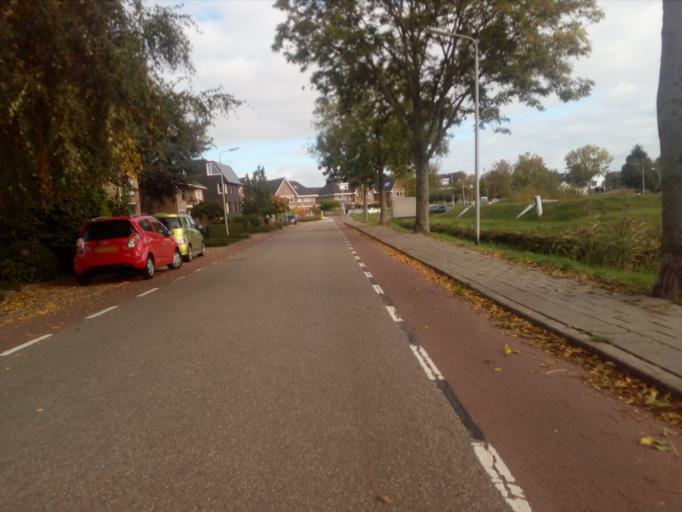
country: NL
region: South Holland
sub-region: Gemeente Lansingerland
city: Berkel en Rodenrijs
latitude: 51.9979
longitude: 4.4782
